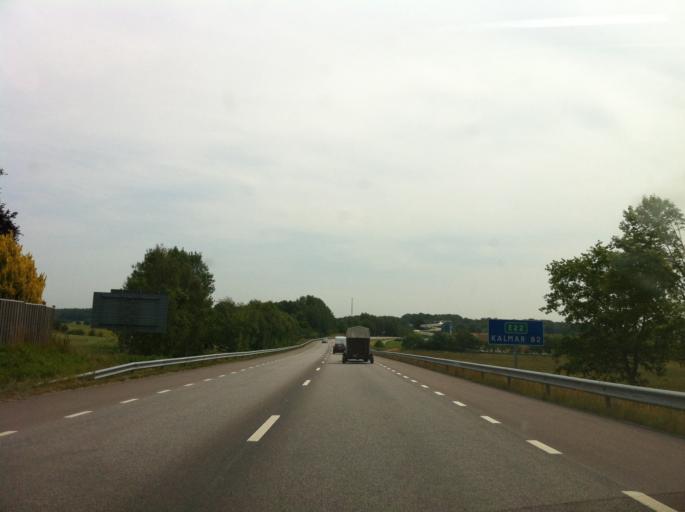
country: SE
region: Blekinge
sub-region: Karlskrona Kommun
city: Rodeby
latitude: 56.1983
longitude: 15.6846
